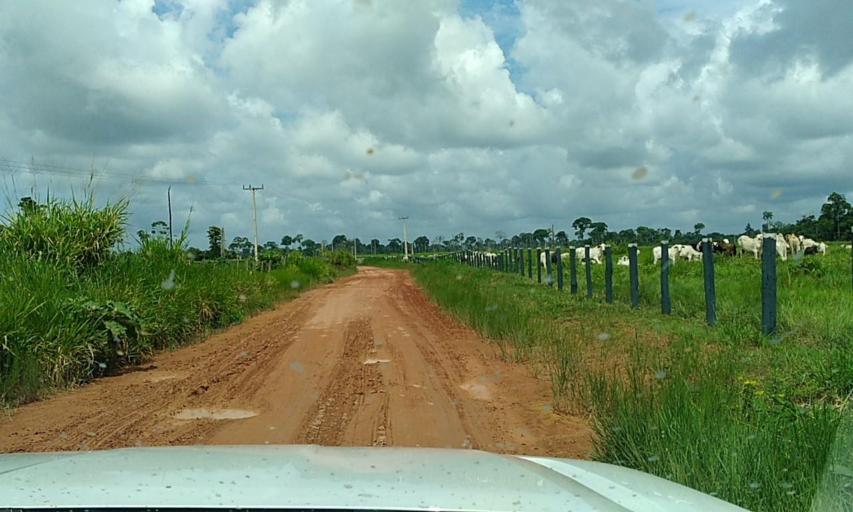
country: BR
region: Para
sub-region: Senador Jose Porfirio
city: Senador Jose Porfirio
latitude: -2.5162
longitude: -51.8445
